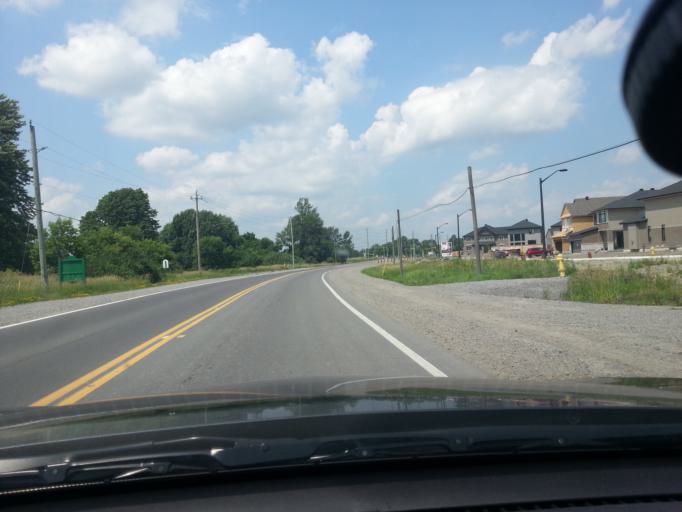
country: CA
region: Ontario
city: Bells Corners
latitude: 45.2659
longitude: -75.7011
